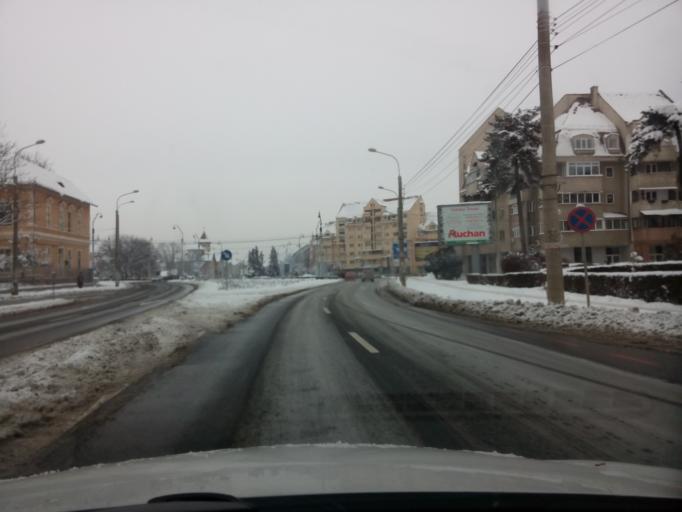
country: RO
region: Sibiu
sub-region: Municipiul Sibiu
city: Sibiu
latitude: 45.7954
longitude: 24.1598
